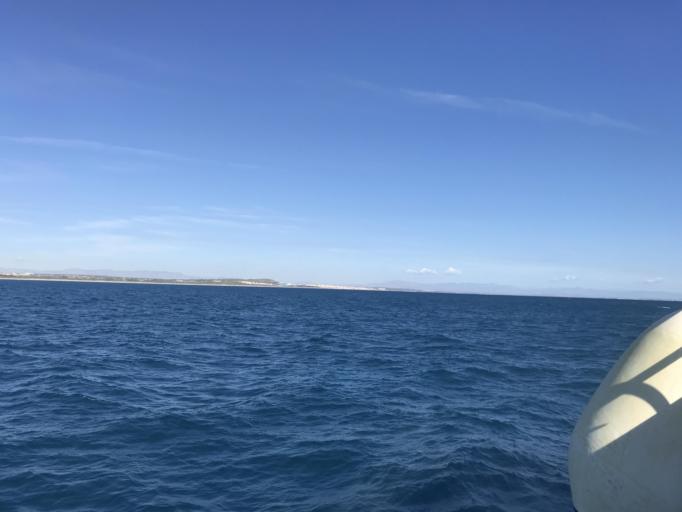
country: ES
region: Valencia
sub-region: Provincia de Alicante
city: Torrevieja
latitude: 38.0146
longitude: -0.6261
